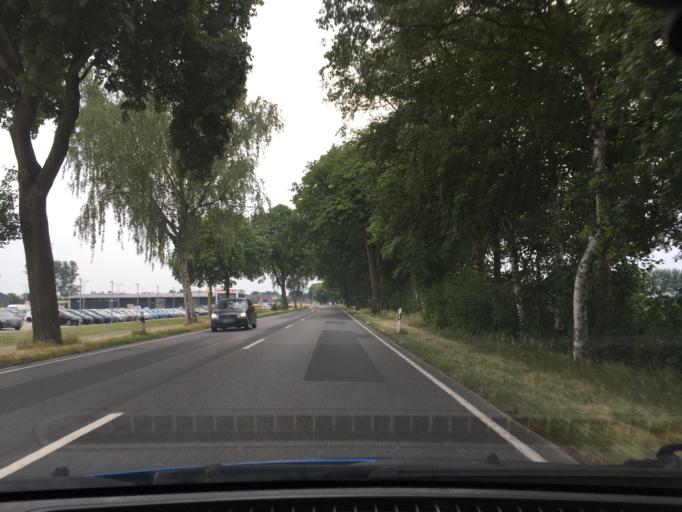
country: DE
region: Lower Saxony
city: Tostedt
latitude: 53.2902
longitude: 9.7283
